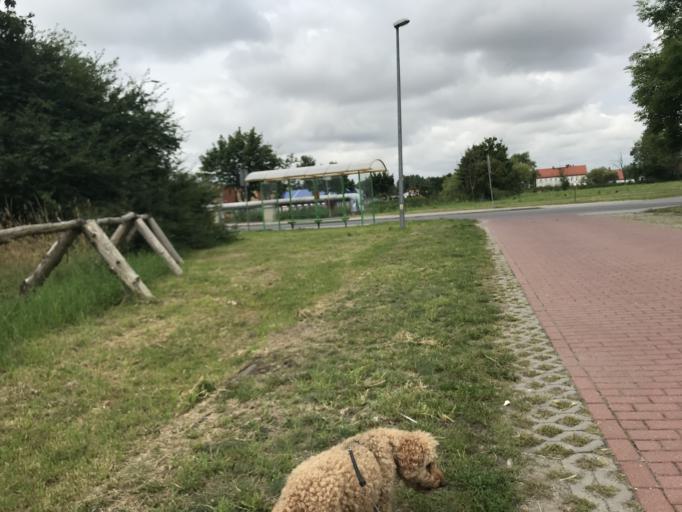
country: PL
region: Warmian-Masurian Voivodeship
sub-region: Powiat elblaski
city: Elblag
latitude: 54.1555
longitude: 19.3915
